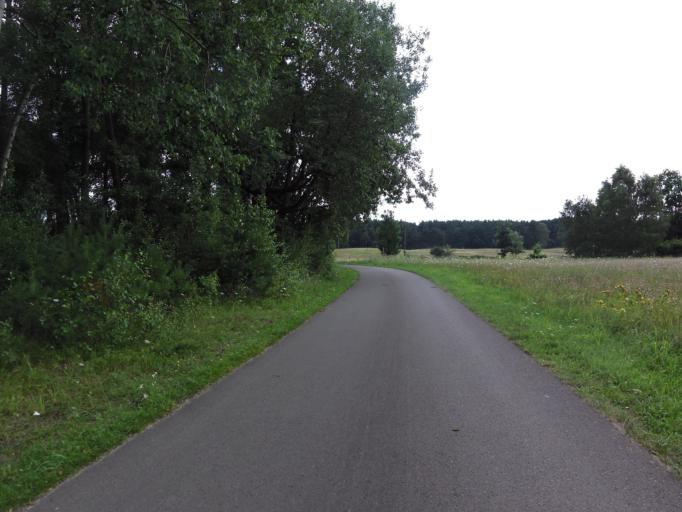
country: DE
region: Brandenburg
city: Lychen
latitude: 53.2666
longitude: 13.3046
